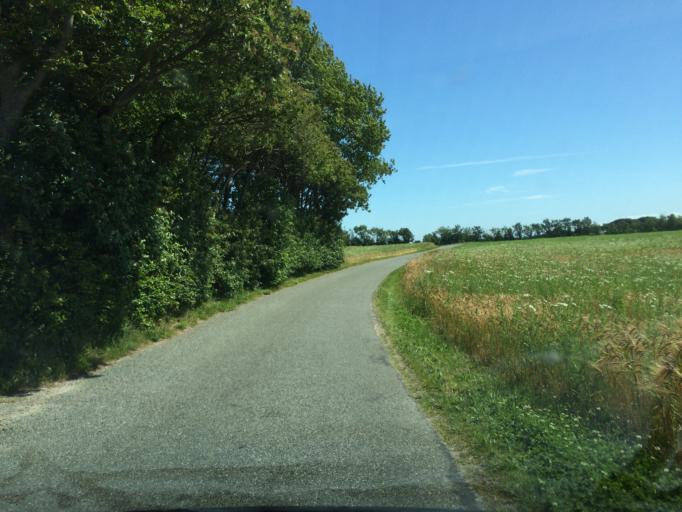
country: DK
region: Central Jutland
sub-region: Samso Kommune
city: Tranebjerg
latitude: 55.8349
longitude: 10.5375
